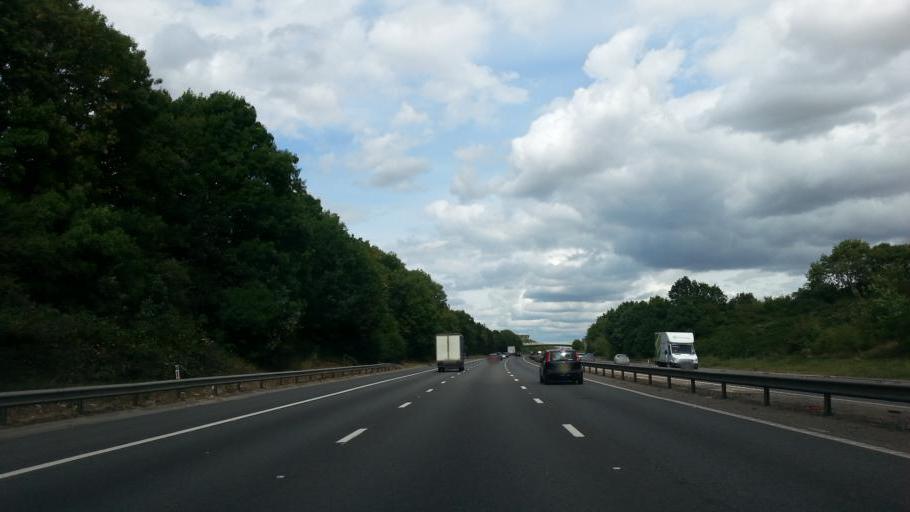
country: GB
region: England
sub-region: Essex
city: Harlow
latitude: 51.7579
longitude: 0.1474
